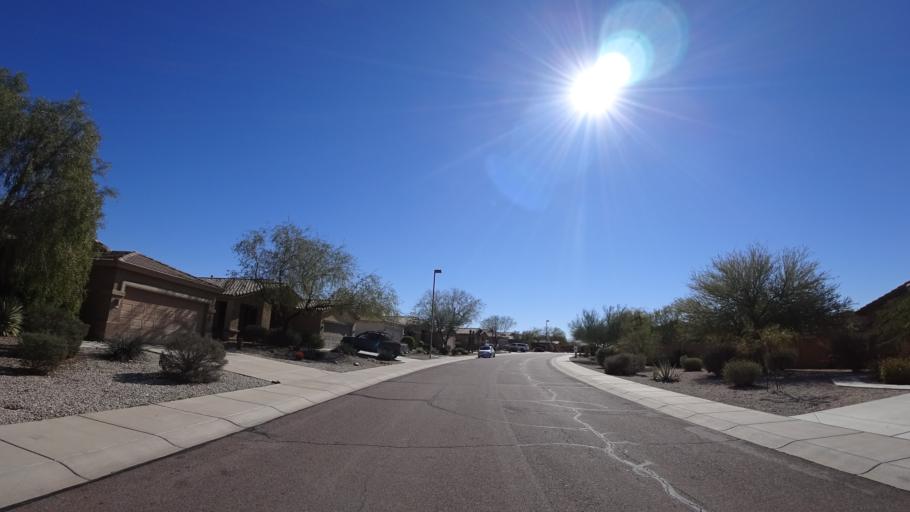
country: US
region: Arizona
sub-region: Maricopa County
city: Goodyear
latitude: 33.3532
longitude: -112.4250
